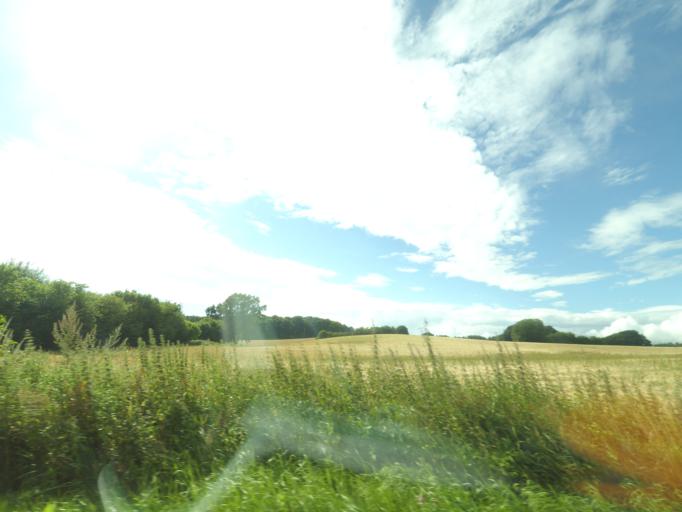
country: DK
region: South Denmark
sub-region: Assens Kommune
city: Vissenbjerg
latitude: 55.4181
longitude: 10.1767
